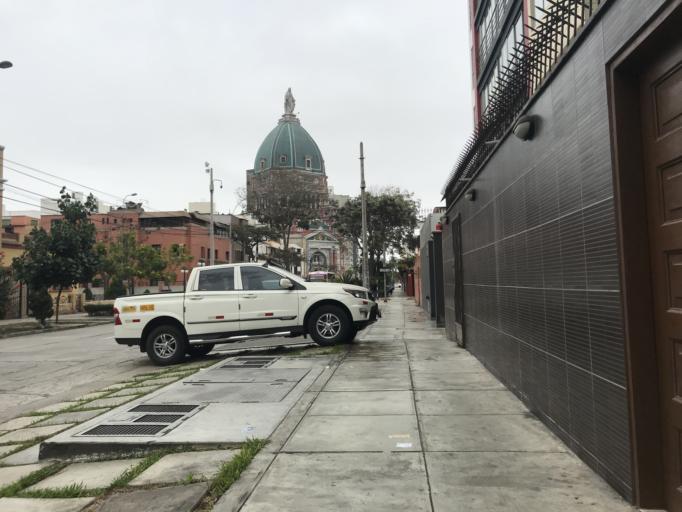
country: PE
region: Lima
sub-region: Lima
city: San Isidro
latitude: -12.0872
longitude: -77.0672
